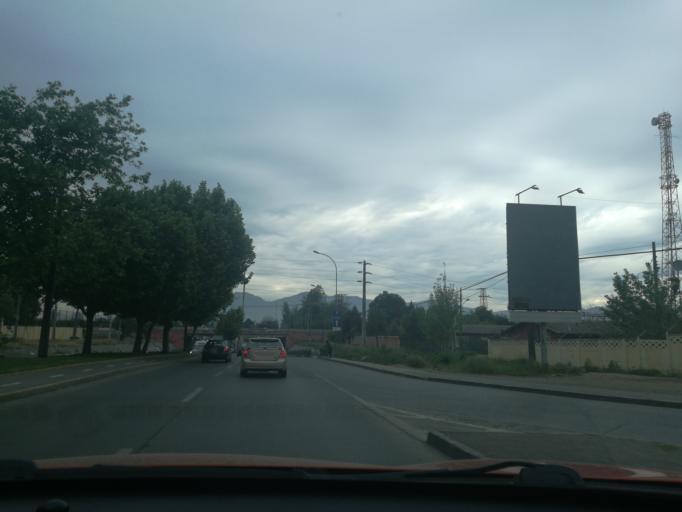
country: CL
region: O'Higgins
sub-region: Provincia de Cachapoal
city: Rancagua
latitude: -34.1675
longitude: -70.7254
